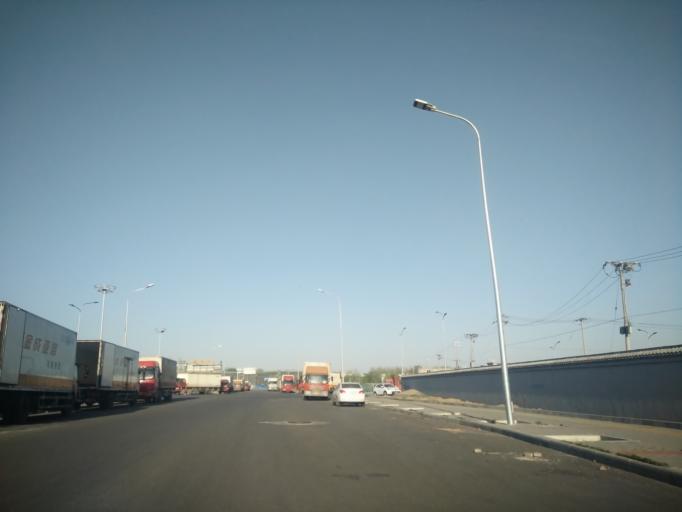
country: CN
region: Beijing
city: Yinghai
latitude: 39.7568
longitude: 116.4380
